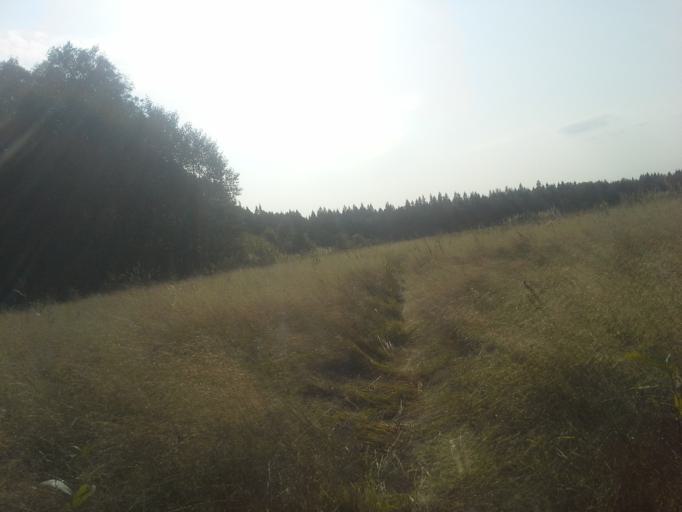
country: RU
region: Moskovskaya
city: Kievskij
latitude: 55.3813
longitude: 36.9425
